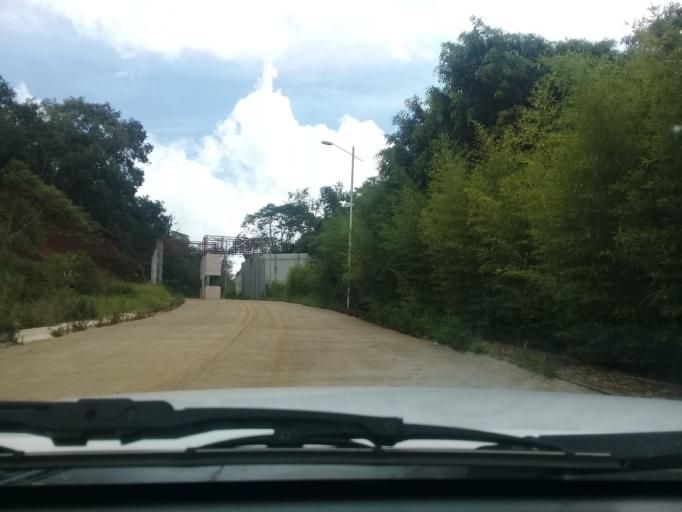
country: MX
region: Veracruz
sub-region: Xalapa
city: Lomas Verdes
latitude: 19.5030
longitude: -96.9124
